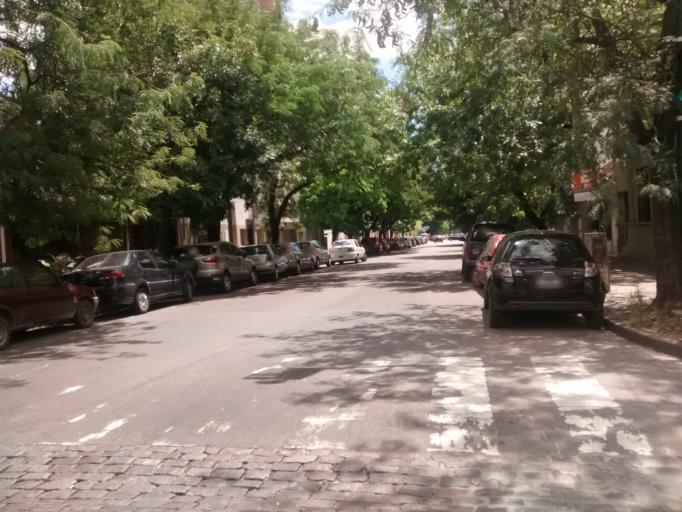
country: AR
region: Buenos Aires
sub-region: Partido de La Plata
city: La Plata
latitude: -34.9162
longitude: -57.9591
